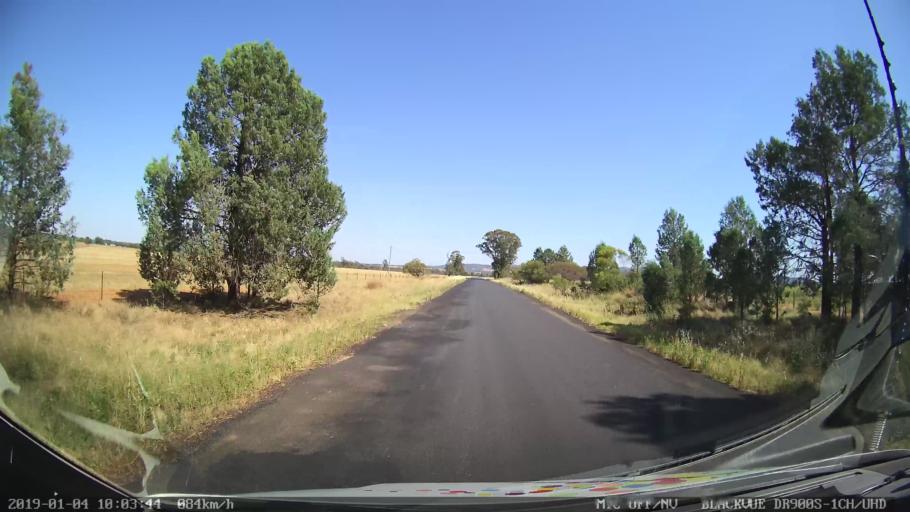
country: AU
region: New South Wales
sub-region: Cabonne
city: Canowindra
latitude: -33.4602
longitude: 148.3632
